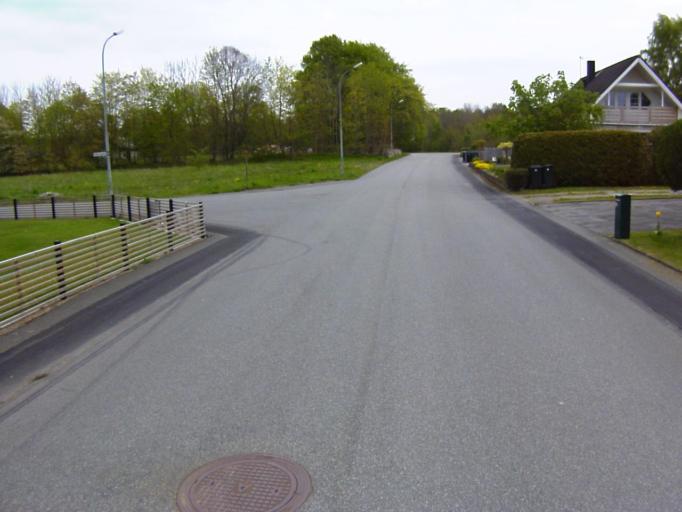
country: SE
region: Skane
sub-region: Kristianstads Kommun
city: Onnestad
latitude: 55.9355
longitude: 13.9873
